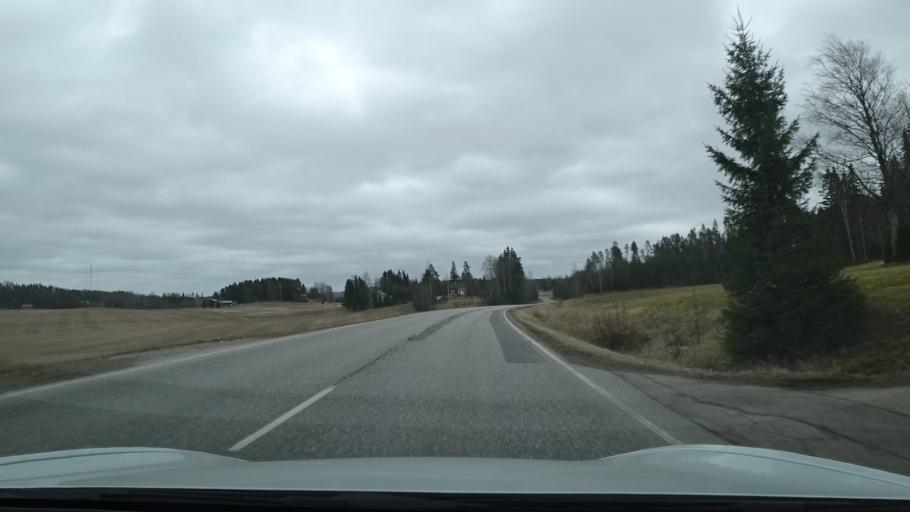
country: FI
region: Uusimaa
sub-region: Porvoo
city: Myrskylae
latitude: 60.6592
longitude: 25.8234
